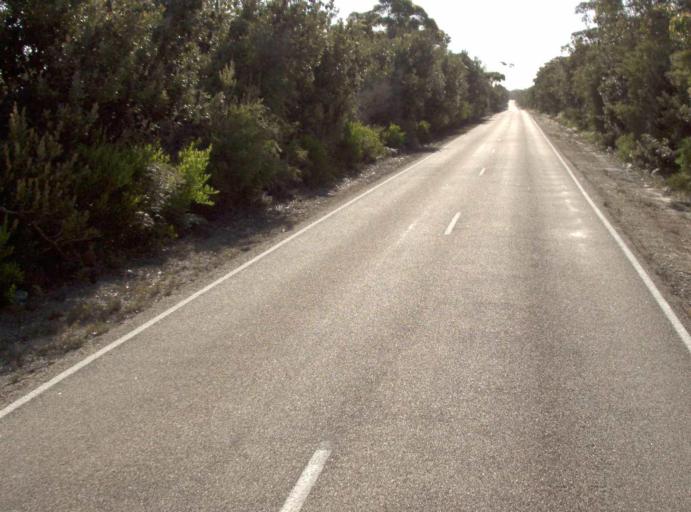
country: AU
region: Victoria
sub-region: East Gippsland
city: Lakes Entrance
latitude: -37.7975
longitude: 148.7103
